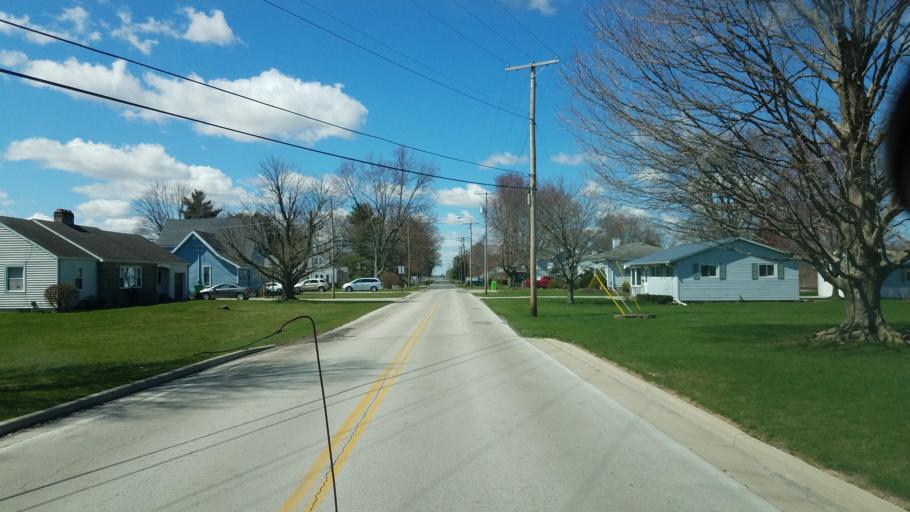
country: US
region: Ohio
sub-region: Seneca County
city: Fostoria
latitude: 41.1562
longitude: -83.4348
